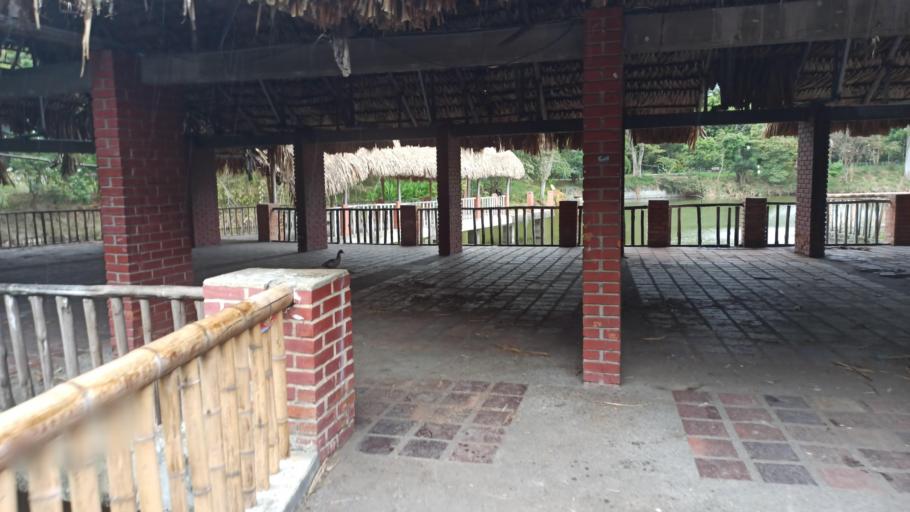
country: CO
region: Valle del Cauca
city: Palmira
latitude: 3.5280
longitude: -76.2875
